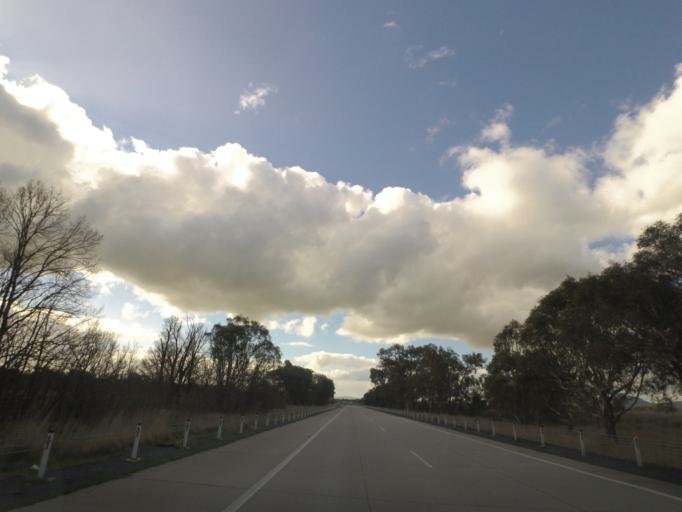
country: AU
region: New South Wales
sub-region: Greater Hume Shire
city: Holbrook
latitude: -35.7424
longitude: 147.3018
